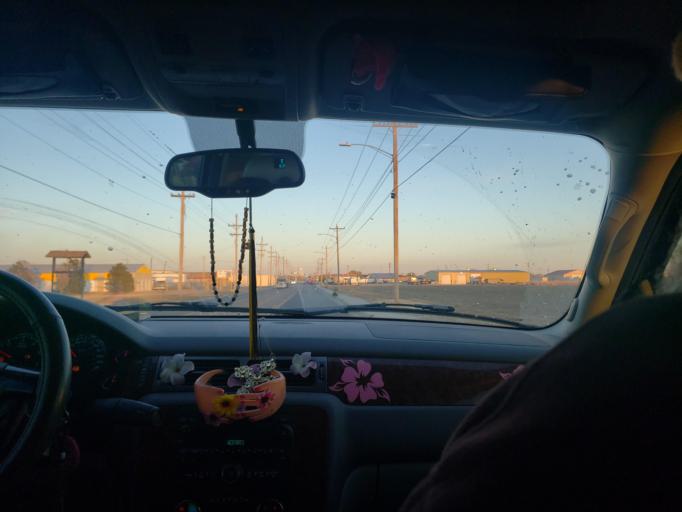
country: US
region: Kansas
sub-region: Finney County
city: Garden City
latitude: 37.9892
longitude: -100.8872
